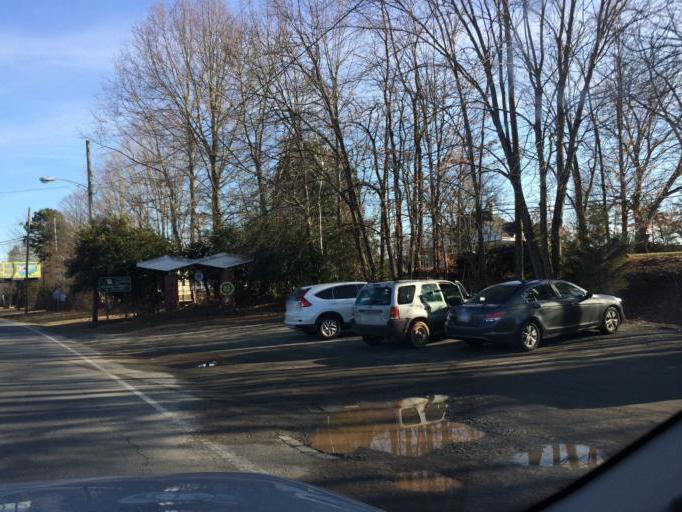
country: US
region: North Carolina
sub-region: Rutherford County
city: Forest City
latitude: 35.3411
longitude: -81.8800
